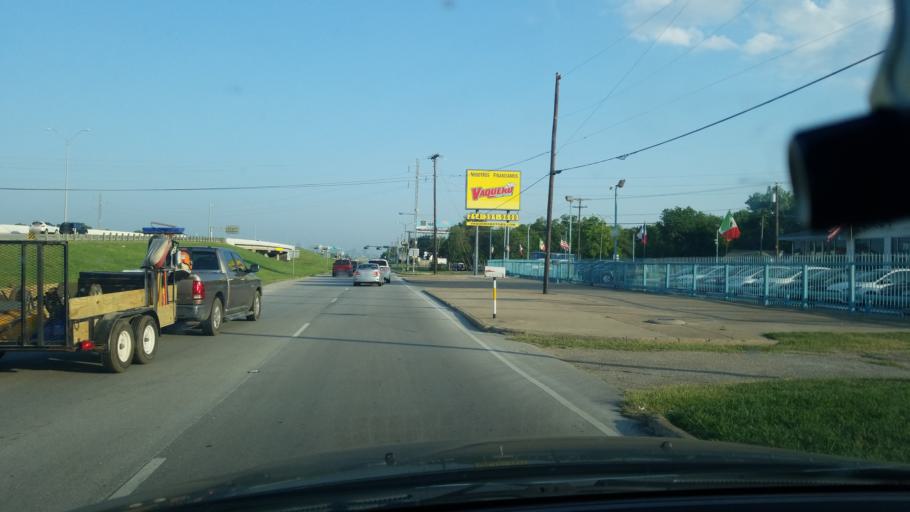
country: US
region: Texas
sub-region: Dallas County
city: Balch Springs
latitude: 32.7188
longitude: -96.6913
